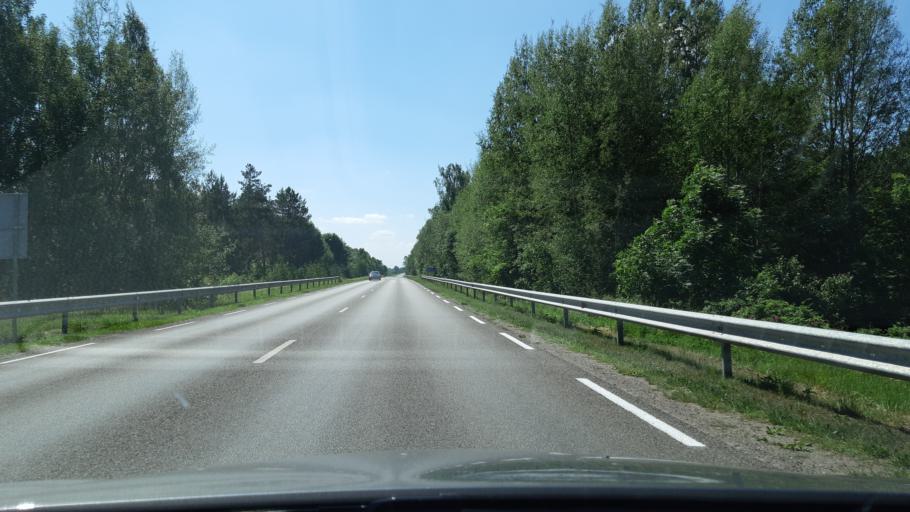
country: LT
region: Alytaus apskritis
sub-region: Alytus
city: Alytus
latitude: 54.4446
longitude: 24.1160
